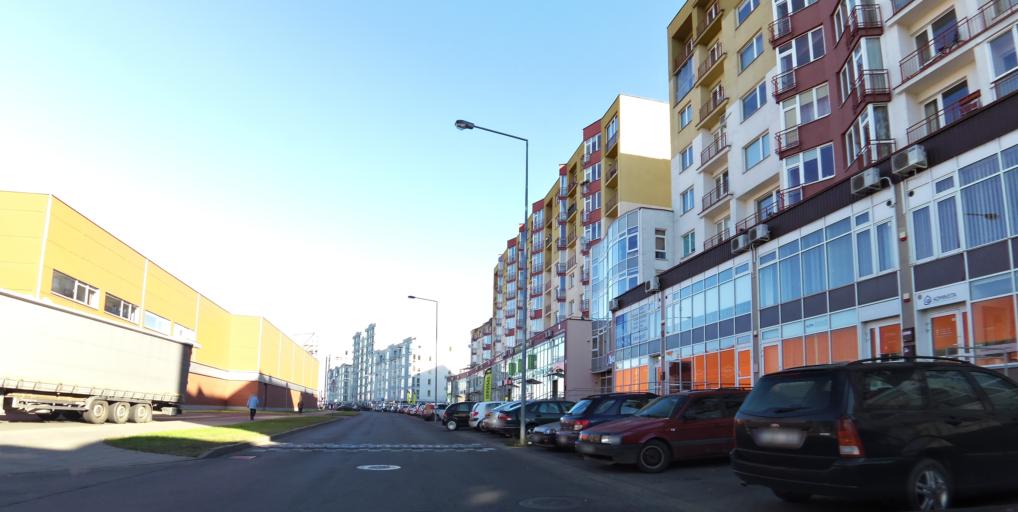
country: LT
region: Vilnius County
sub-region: Vilnius
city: Vilnius
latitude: 54.7085
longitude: 25.3023
